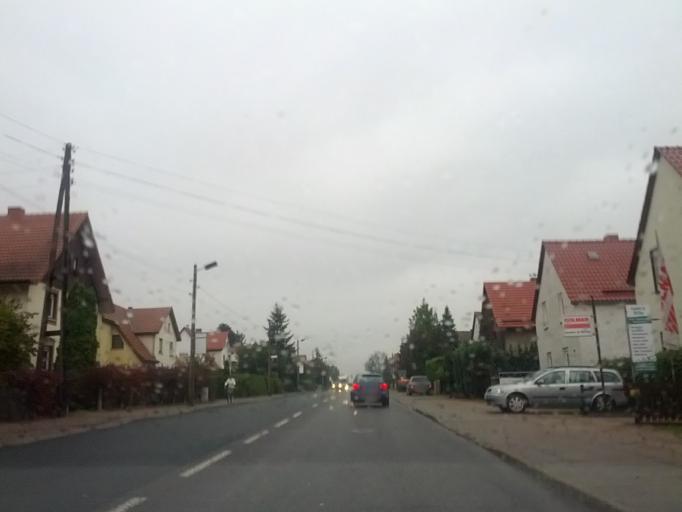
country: DE
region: Thuringia
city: Gotha
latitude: 50.9349
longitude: 10.7161
